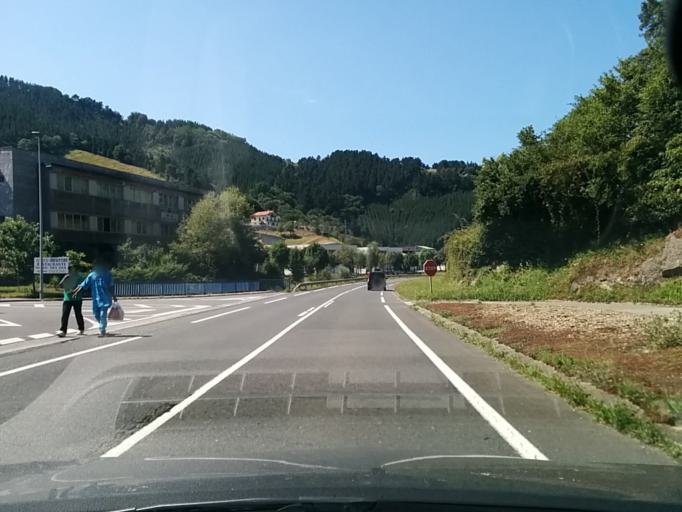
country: ES
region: Basque Country
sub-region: Bizkaia
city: Ondarroa
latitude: 43.3104
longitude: -2.4089
